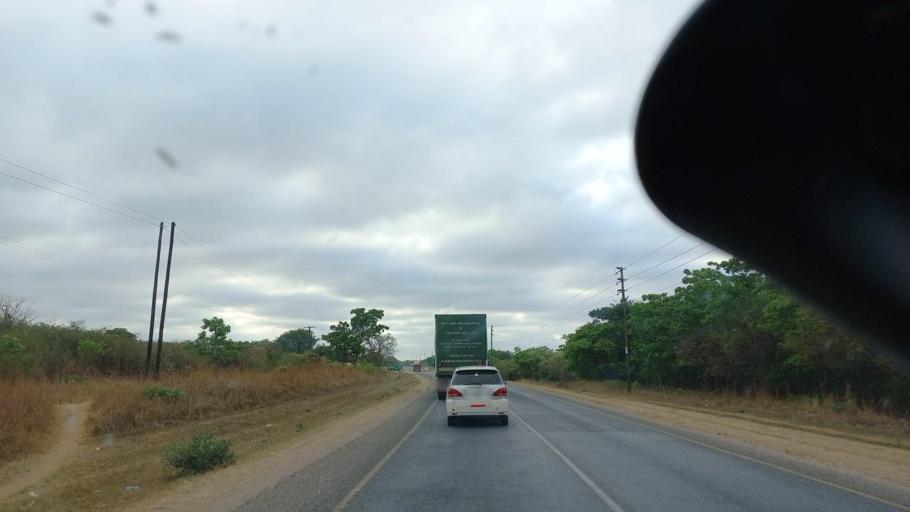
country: ZM
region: Lusaka
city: Chongwe
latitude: -15.3473
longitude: 28.5294
